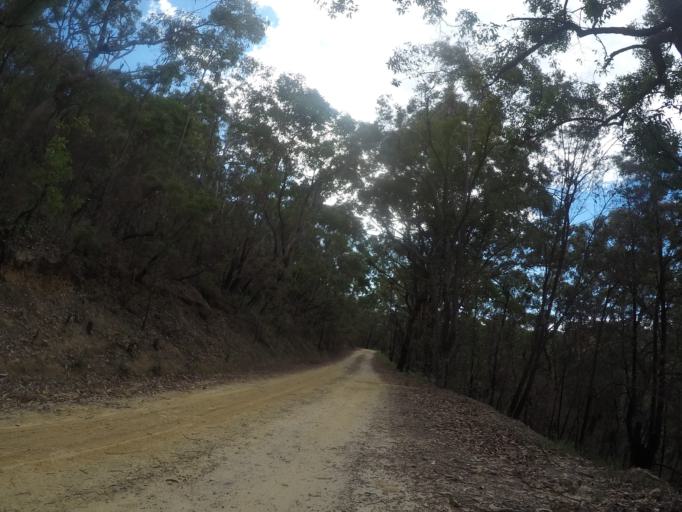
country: AU
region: New South Wales
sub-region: Hornsby Shire
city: Glenorie
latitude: -33.3737
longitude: 151.0468
